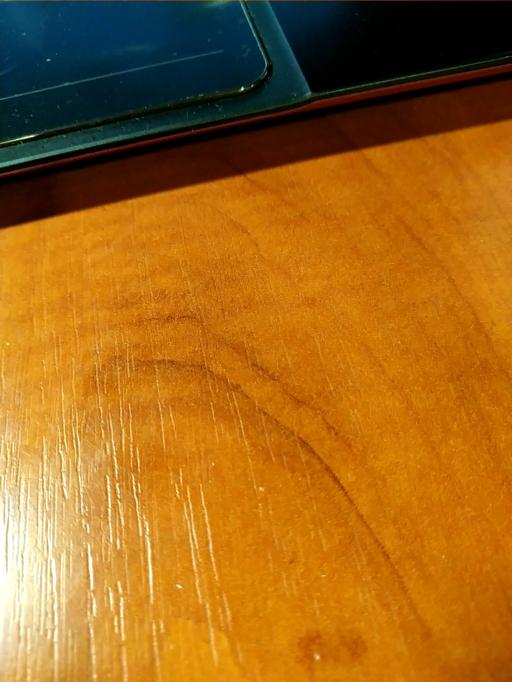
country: RU
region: Tverskaya
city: Zubtsov
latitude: 56.1597
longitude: 34.6033
